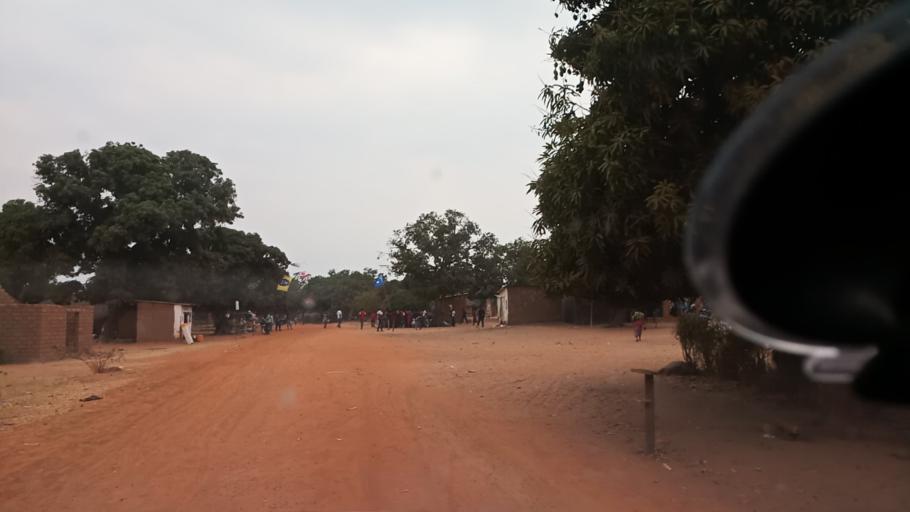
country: ZM
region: Luapula
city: Nchelenge
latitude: -9.1837
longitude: 28.2830
